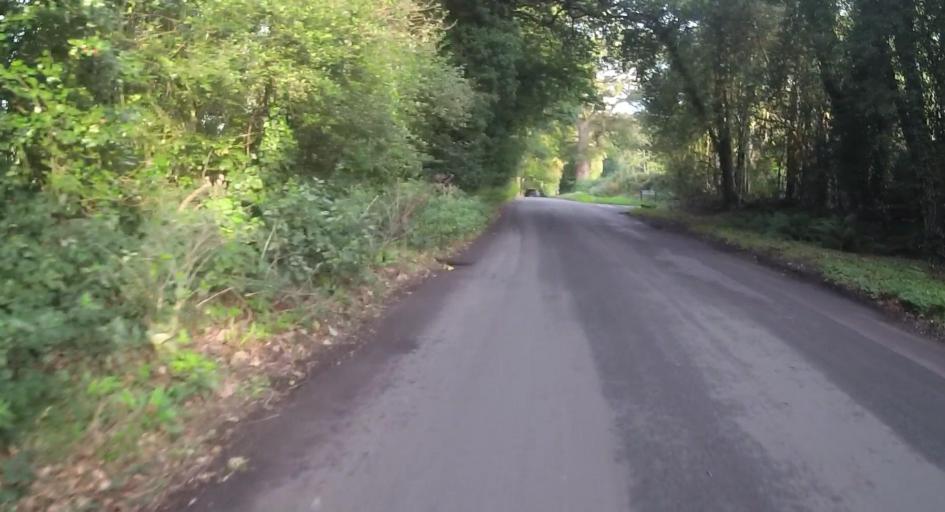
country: GB
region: England
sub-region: West Berkshire
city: Thatcham
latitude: 51.4118
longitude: -1.1931
